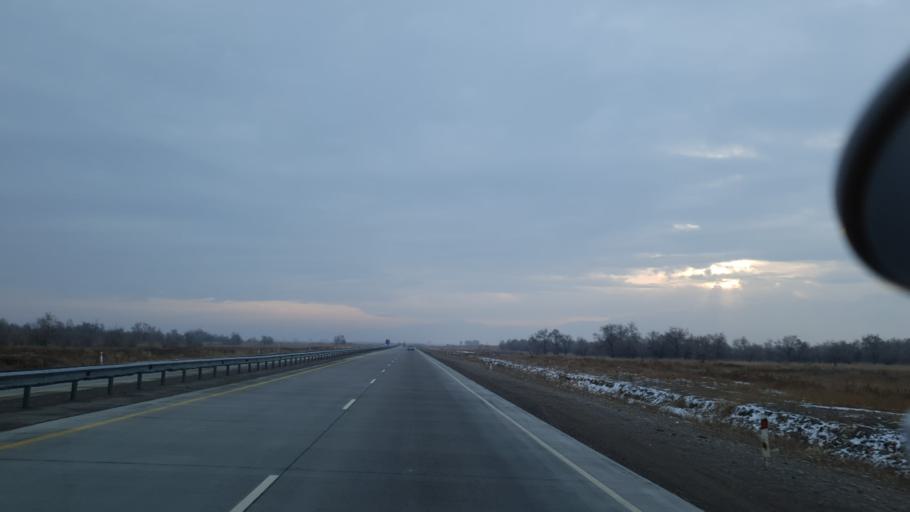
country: KZ
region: Almaty Oblysy
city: Energeticheskiy
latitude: 43.4664
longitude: 77.0866
